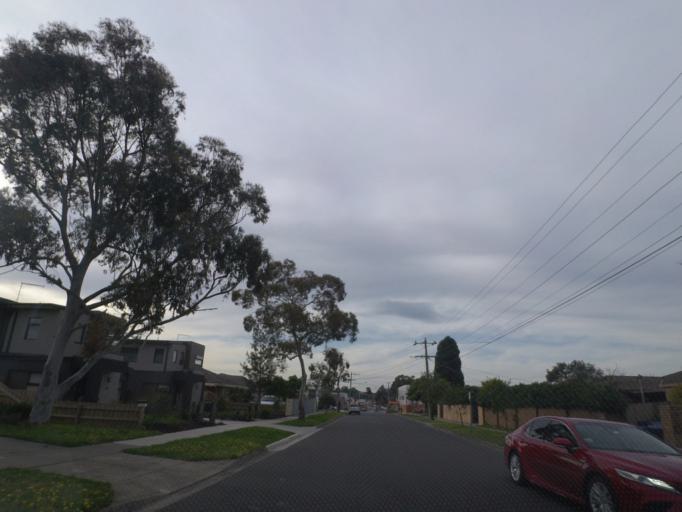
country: AU
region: Victoria
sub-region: Knox
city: Ferntree Gully
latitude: -37.8852
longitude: 145.2760
